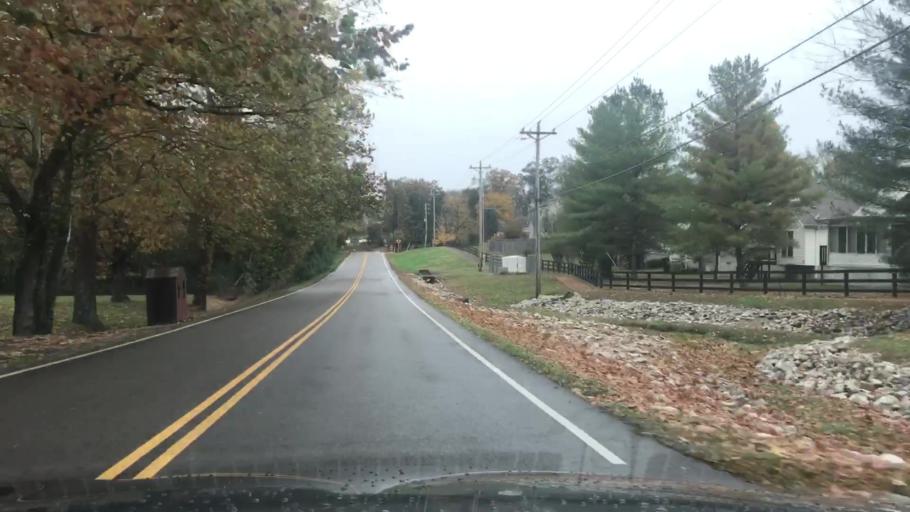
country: US
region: Tennessee
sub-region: Williamson County
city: Franklin
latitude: 35.8974
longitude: -86.8226
